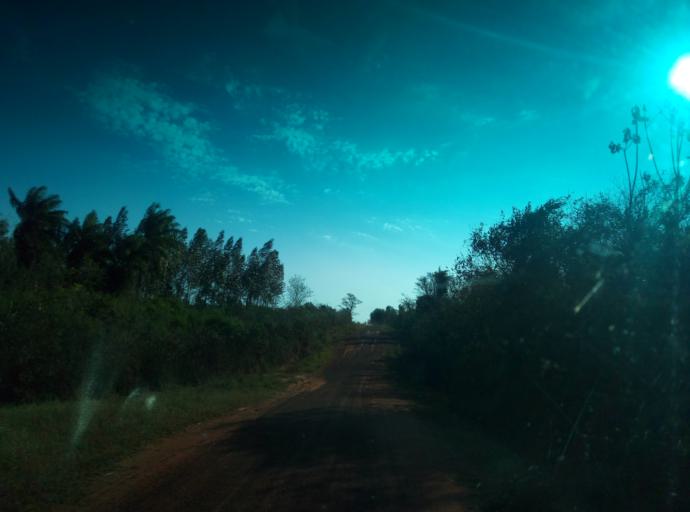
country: PY
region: Caaguazu
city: Doctor Cecilio Baez
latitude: -25.1648
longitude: -56.2263
